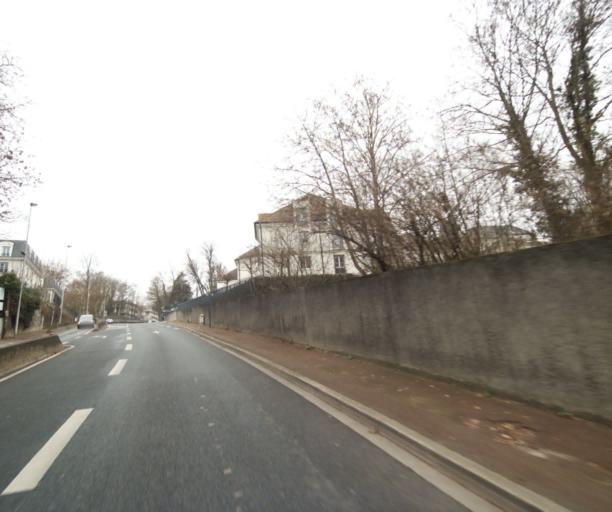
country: FR
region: Ile-de-France
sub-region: Departement des Yvelines
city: Bougival
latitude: 48.8660
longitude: 2.1544
